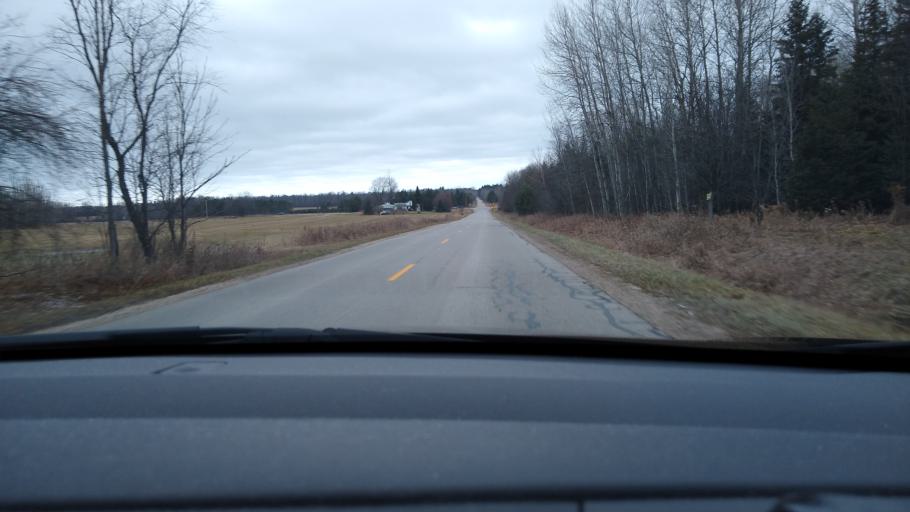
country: US
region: Michigan
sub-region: Missaukee County
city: Lake City
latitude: 44.3331
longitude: -85.0550
